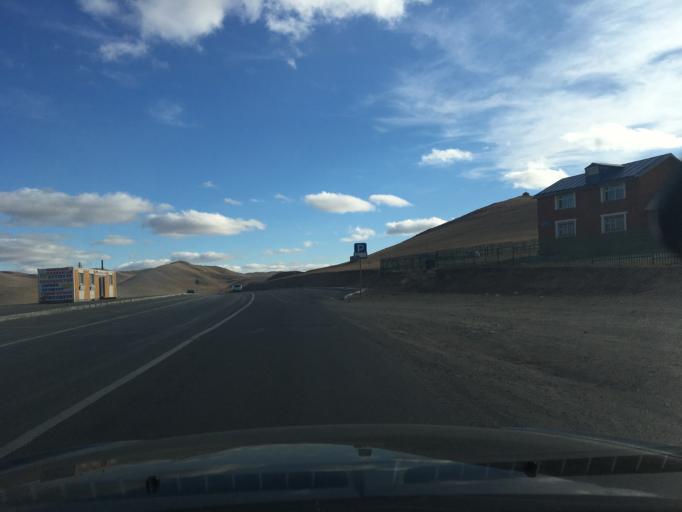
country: MN
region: Ulaanbaatar
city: Ulaanbaatar
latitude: 47.7892
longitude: 106.7465
